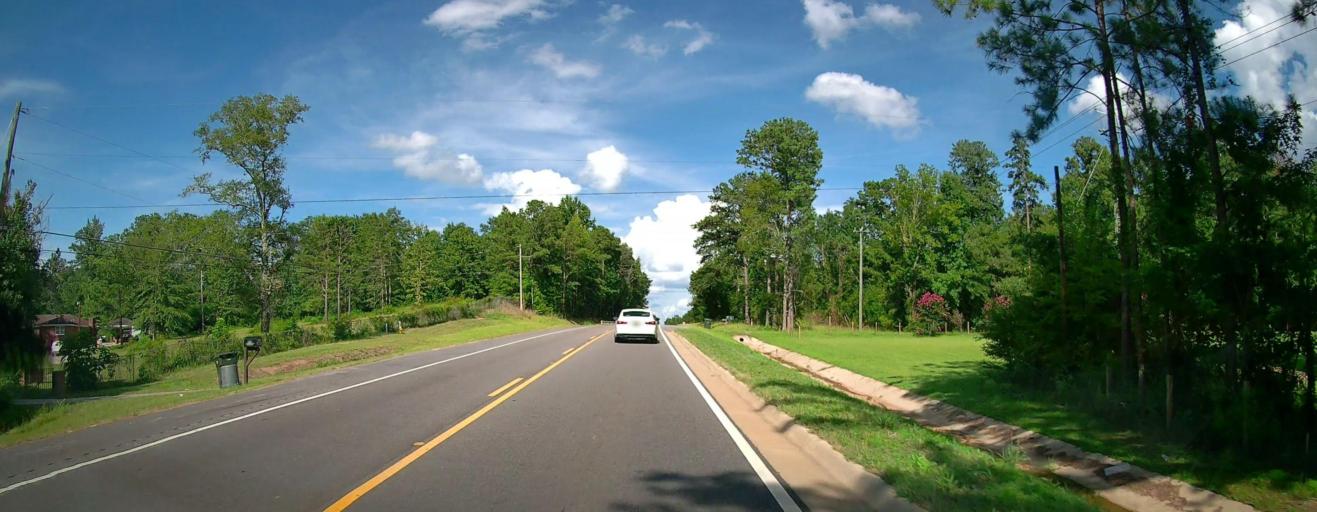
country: US
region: Alabama
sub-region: Russell County
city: Ladonia
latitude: 32.4622
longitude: -85.1293
